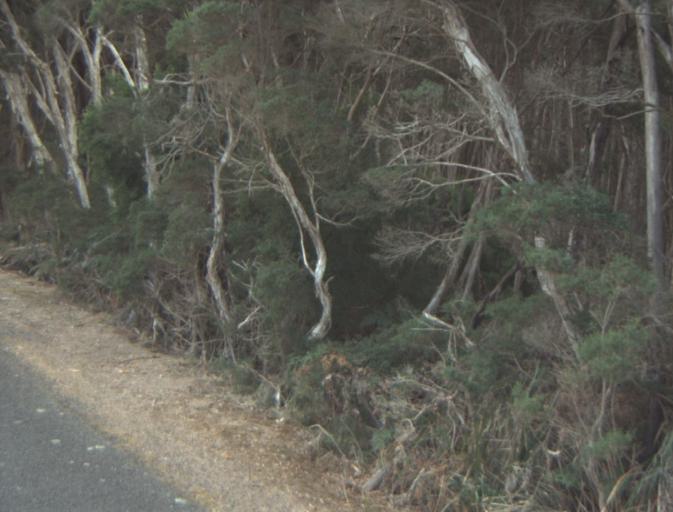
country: AU
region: Tasmania
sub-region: Launceston
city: Mayfield
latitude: -41.2946
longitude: 147.0281
